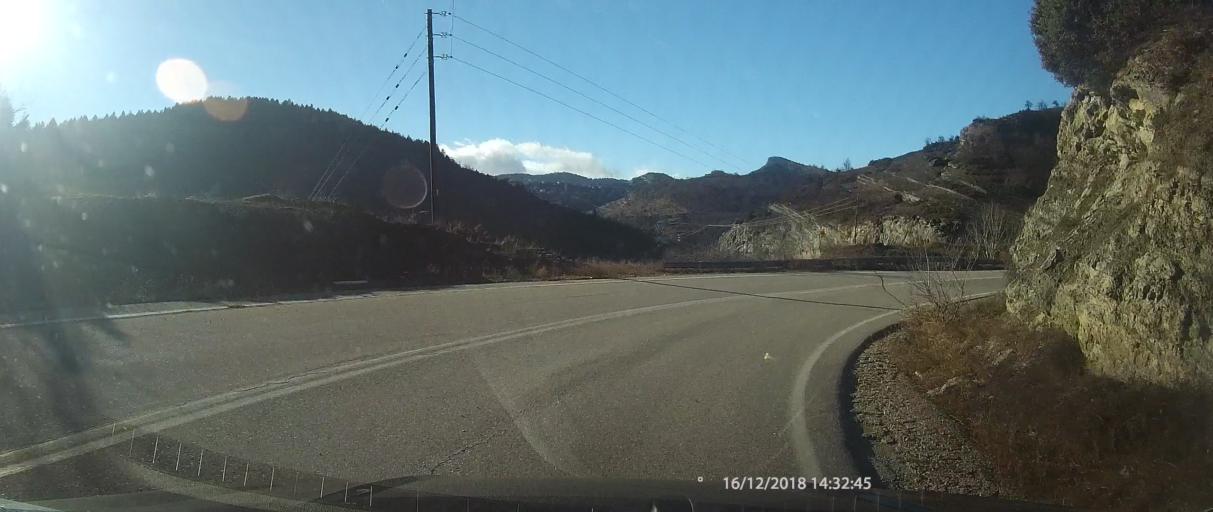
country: GR
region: West Macedonia
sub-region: Nomos Kozanis
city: Tsotili
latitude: 40.1961
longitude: 21.1671
